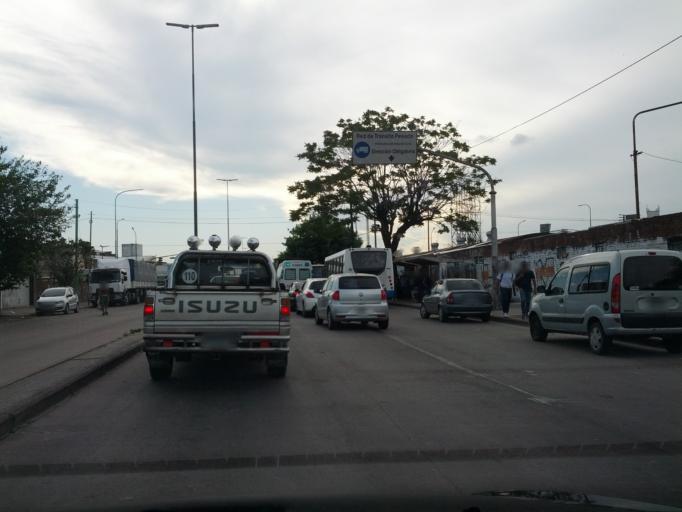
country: AR
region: Buenos Aires
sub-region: Partido de Avellaneda
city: Avellaneda
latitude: -34.6496
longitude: -58.4151
